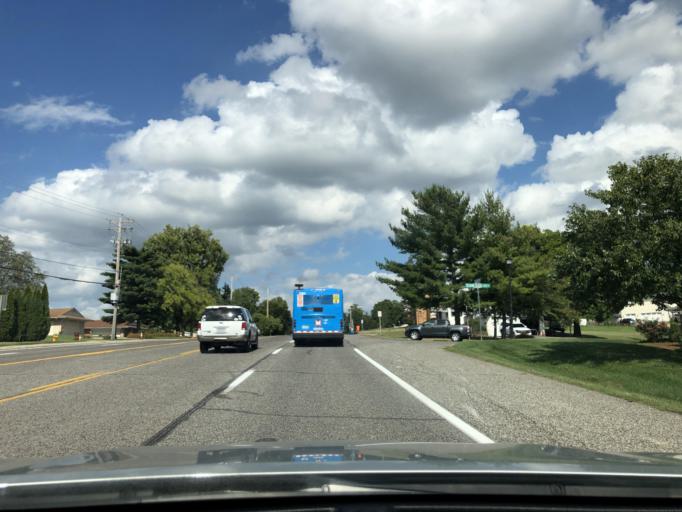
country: US
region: Missouri
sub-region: Saint Louis County
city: Lakeshire
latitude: 38.5369
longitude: -90.3372
